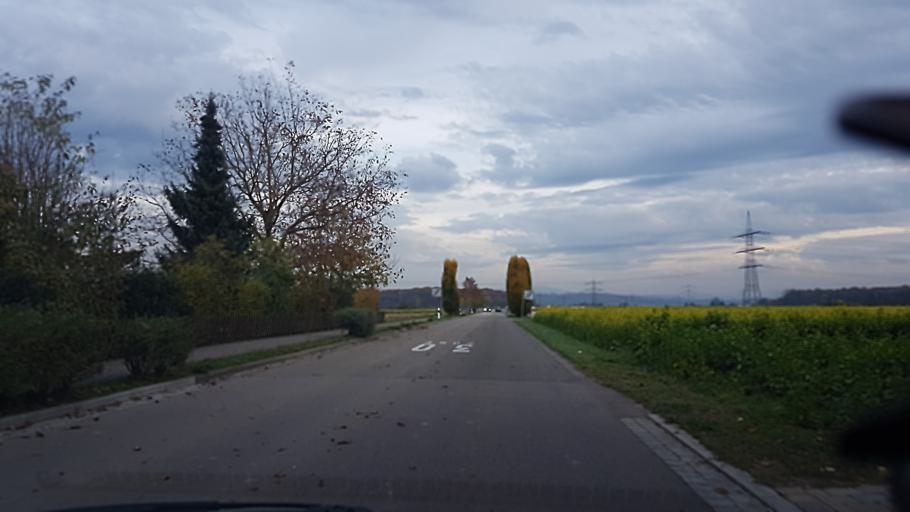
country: DE
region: Baden-Wuerttemberg
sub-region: Freiburg Region
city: Rust
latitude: 48.2669
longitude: 7.7362
